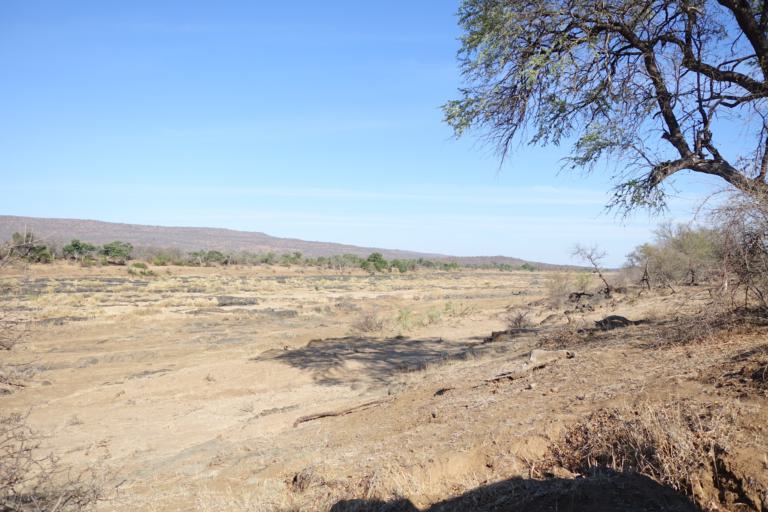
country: ZA
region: Limpopo
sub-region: Mopani District Municipality
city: Phalaborwa
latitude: -23.8847
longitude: 31.6489
